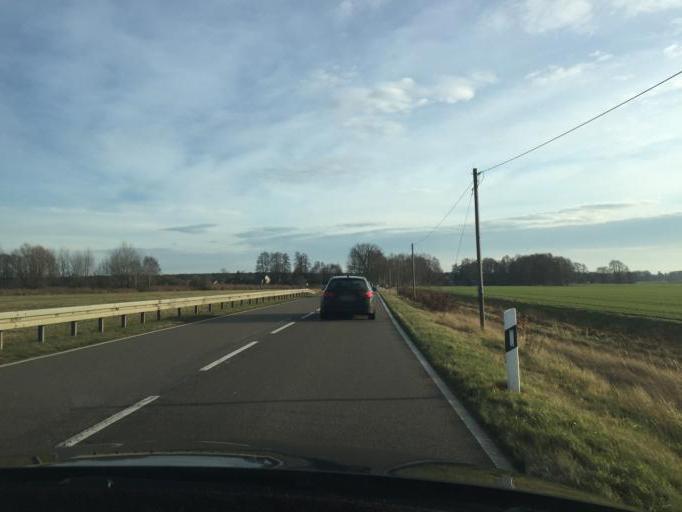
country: DE
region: Brandenburg
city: Heinersbruck
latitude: 51.7287
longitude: 14.4744
